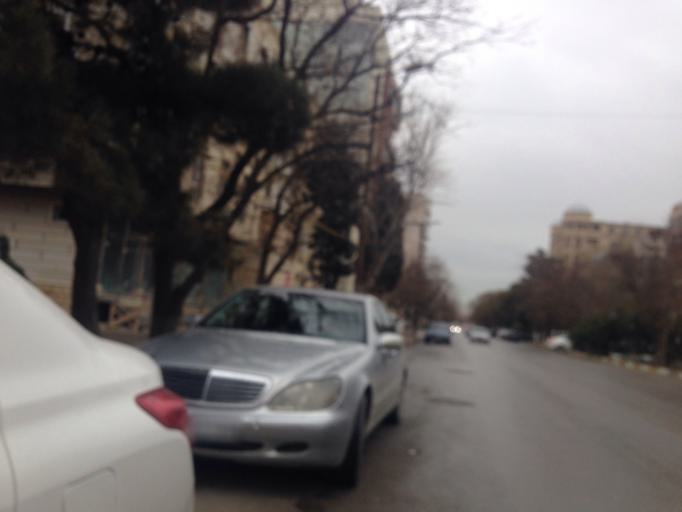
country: AZ
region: Baki
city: Baku
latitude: 40.4085
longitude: 49.8677
